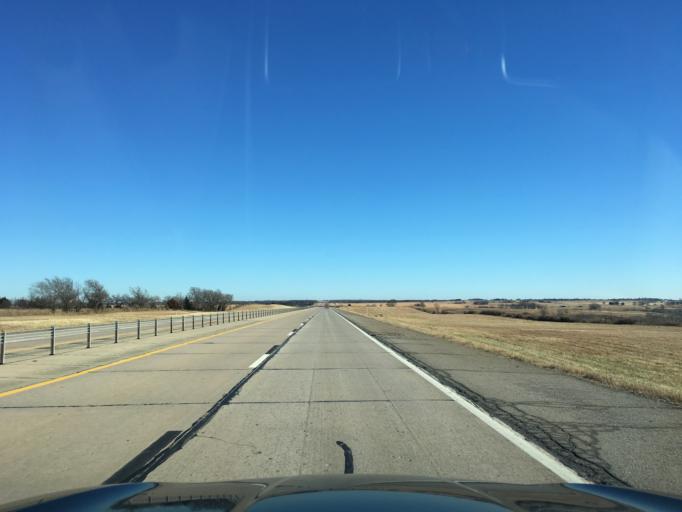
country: US
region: Oklahoma
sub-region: Pawnee County
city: Pawnee
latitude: 36.2253
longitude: -96.8672
